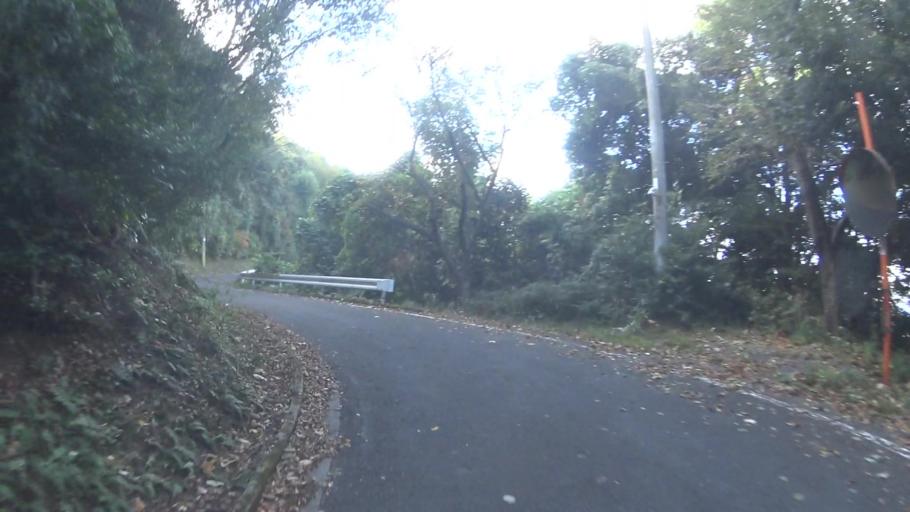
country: JP
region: Kyoto
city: Maizuru
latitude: 35.5677
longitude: 135.4151
